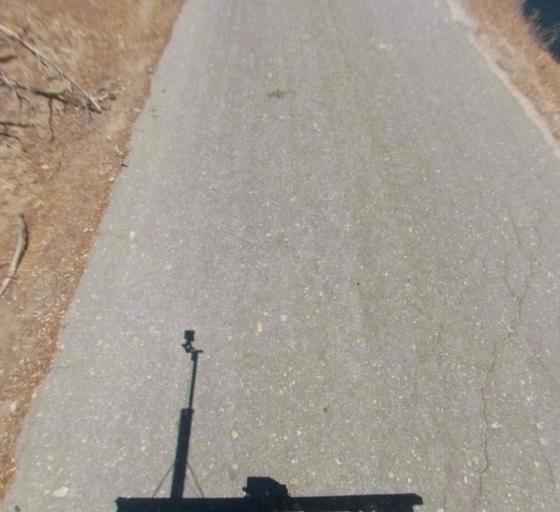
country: US
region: California
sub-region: Fresno County
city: Auberry
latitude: 37.1456
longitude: -119.4457
